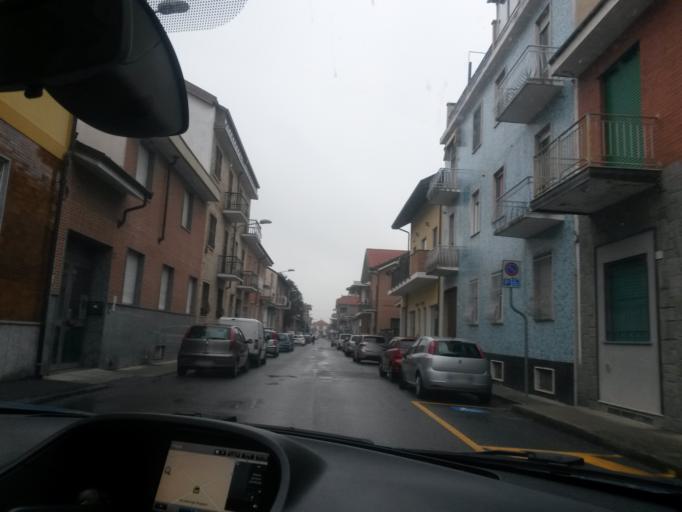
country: IT
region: Piedmont
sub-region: Provincia di Torino
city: Collegno
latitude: 45.0757
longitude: 7.6023
